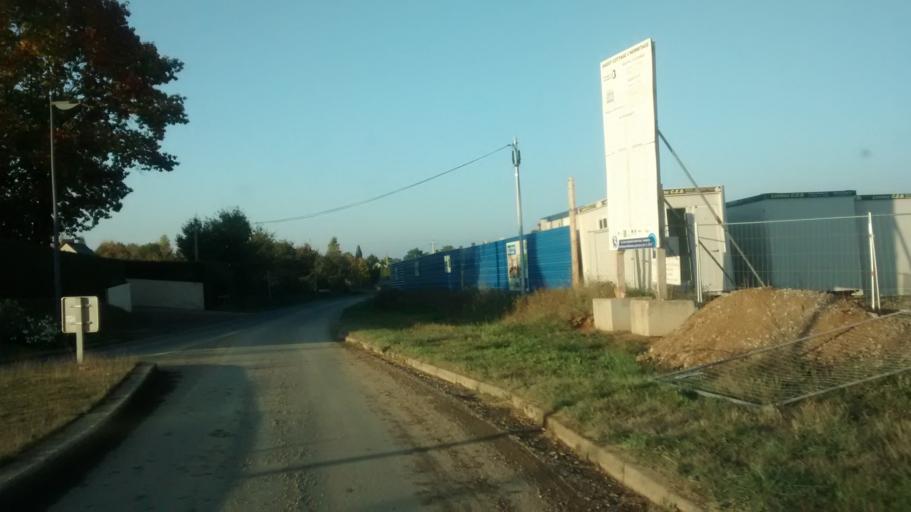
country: FR
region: Brittany
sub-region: Departement d'Ille-et-Vilaine
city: Le Rheu
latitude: 48.1283
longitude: -1.8054
